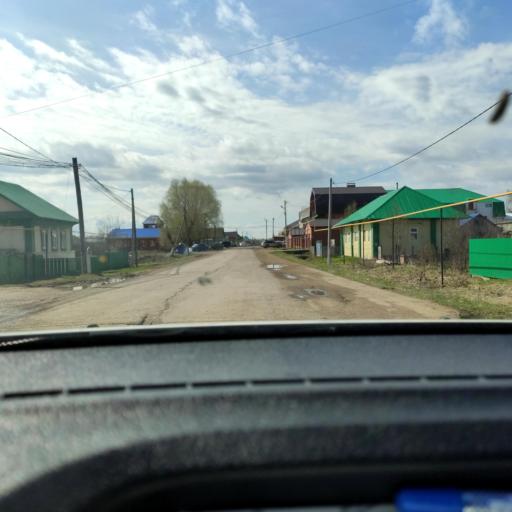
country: RU
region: Bashkortostan
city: Starobaltachevo
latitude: 56.0033
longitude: 55.9320
